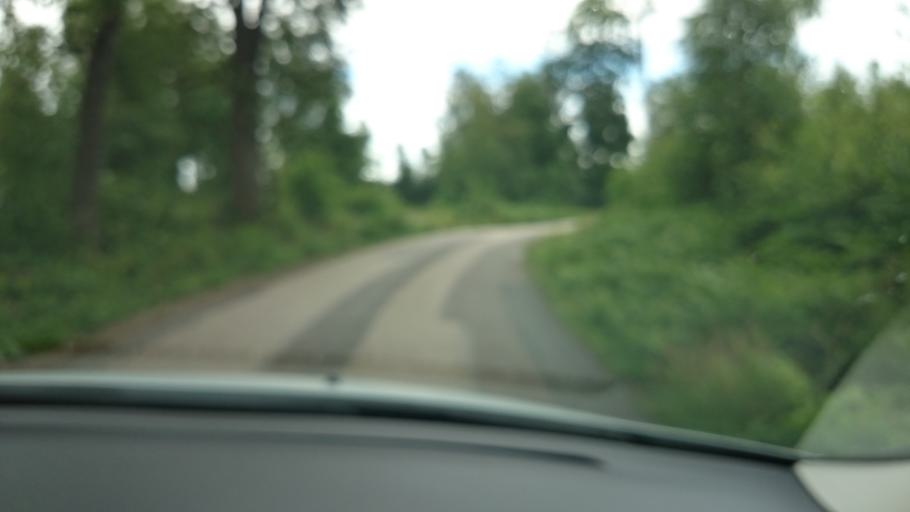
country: SE
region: Halland
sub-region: Hylte Kommun
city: Hyltebruk
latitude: 56.9833
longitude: 13.2260
